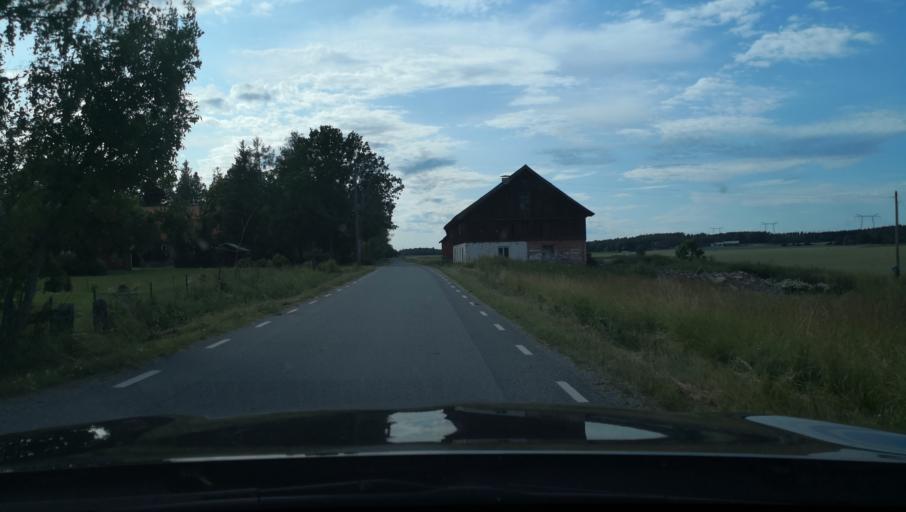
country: SE
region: Uppsala
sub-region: Enkopings Kommun
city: Orsundsbro
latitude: 59.6905
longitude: 17.3626
